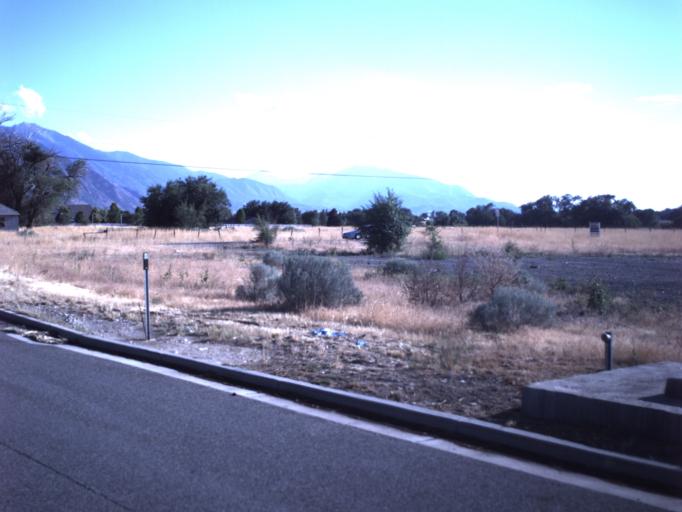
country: US
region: Utah
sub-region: Utah County
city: Mapleton
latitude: 40.1381
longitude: -111.5982
